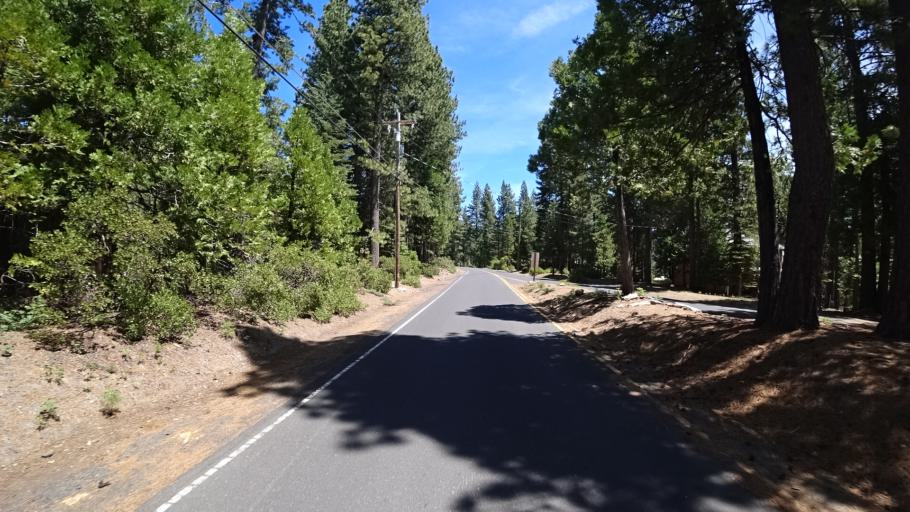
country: US
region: California
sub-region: Calaveras County
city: Arnold
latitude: 38.3149
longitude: -120.2547
